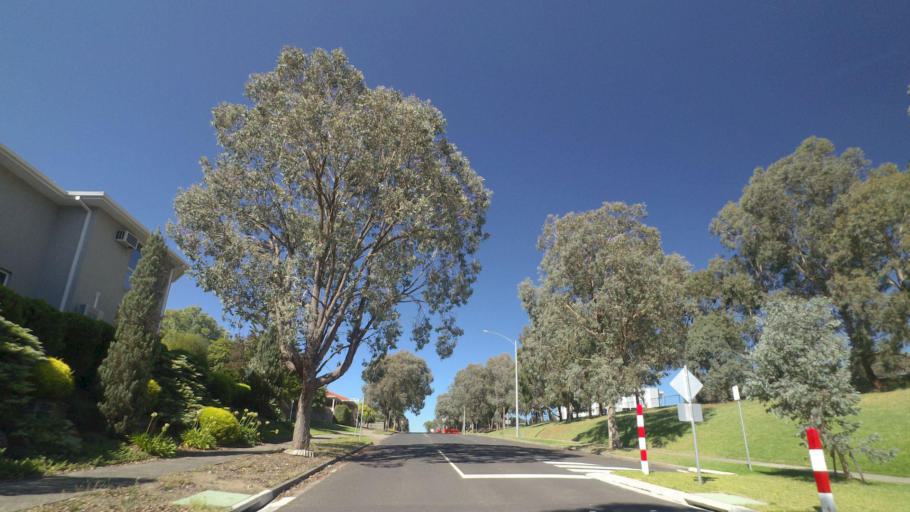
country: AU
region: Victoria
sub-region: Manningham
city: Donvale
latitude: -37.7723
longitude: 145.1756
